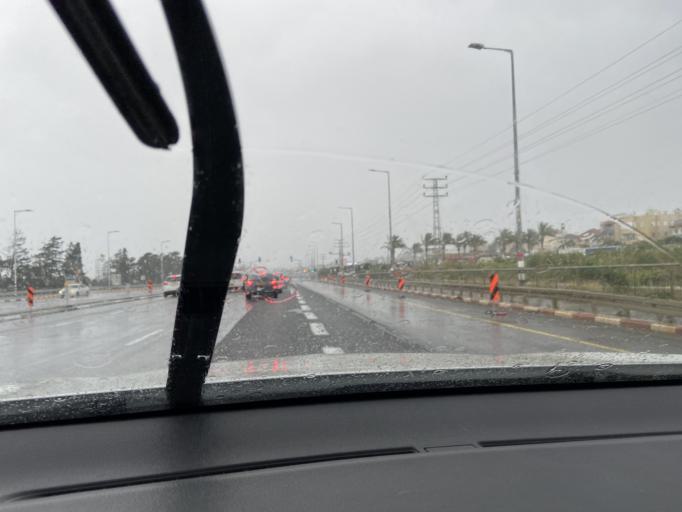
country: IL
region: Northern District
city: El Mazra`a
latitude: 32.9813
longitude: 35.0943
